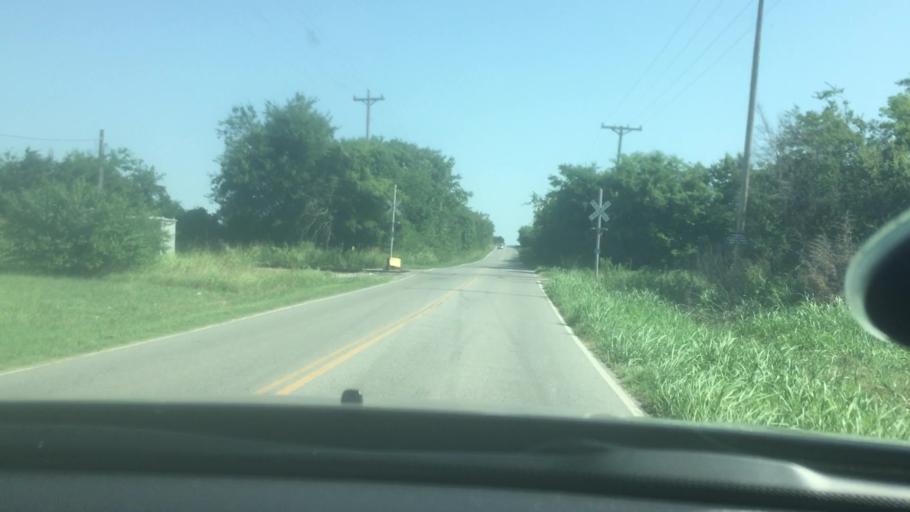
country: US
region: Oklahoma
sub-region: Bryan County
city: Calera
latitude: 34.0085
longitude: -96.4656
